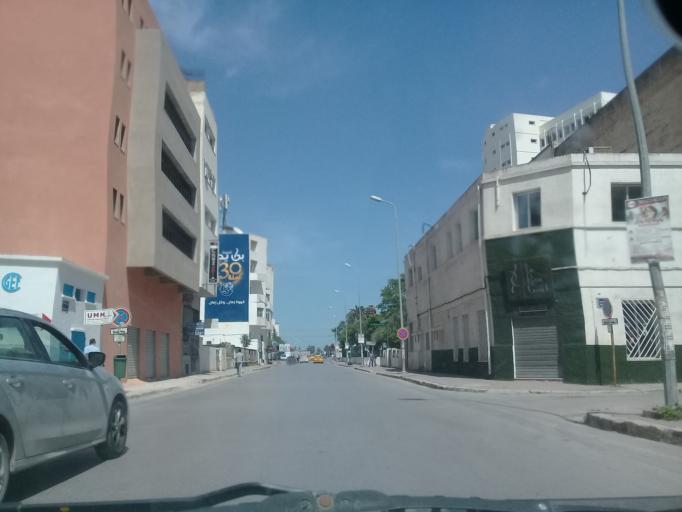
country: TN
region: Tunis
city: Tunis
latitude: 36.8154
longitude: 10.1819
